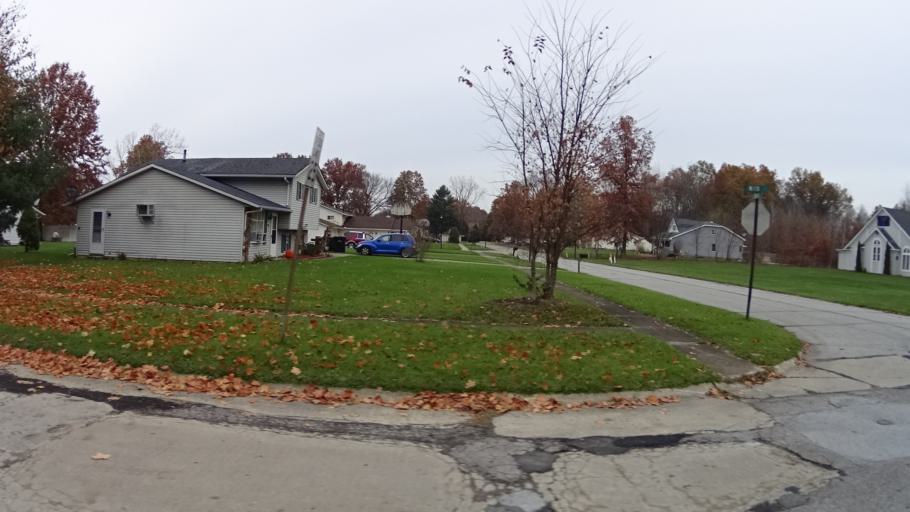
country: US
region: Ohio
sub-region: Lorain County
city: Elyria
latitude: 41.3424
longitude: -82.1035
